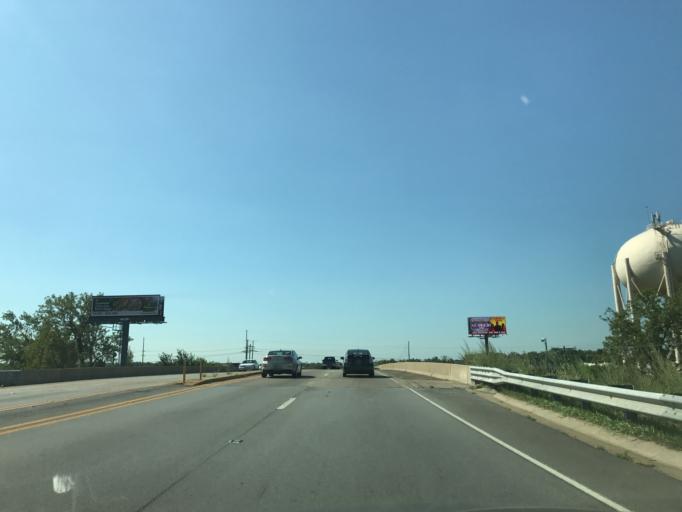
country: US
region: Indiana
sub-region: Lake County
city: Highland
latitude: 41.5324
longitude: -87.4713
